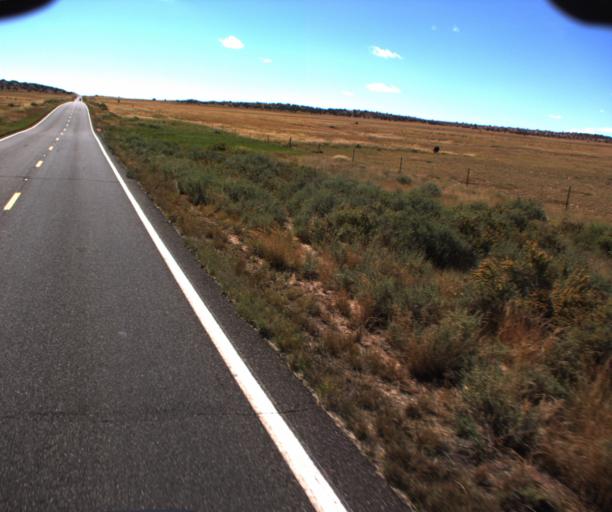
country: US
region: Arizona
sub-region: Apache County
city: Saint Johns
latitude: 34.7688
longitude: -109.2409
